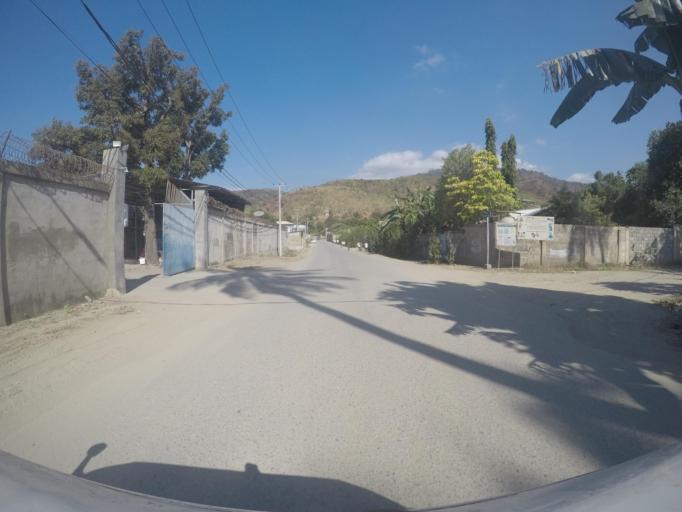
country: TL
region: Dili
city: Dili
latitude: -8.5757
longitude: 125.5342
